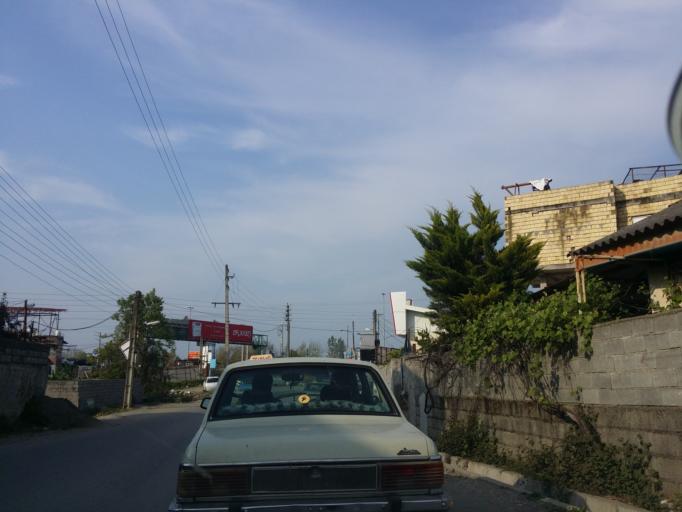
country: IR
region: Mazandaran
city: Chalus
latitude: 36.6595
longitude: 51.3989
